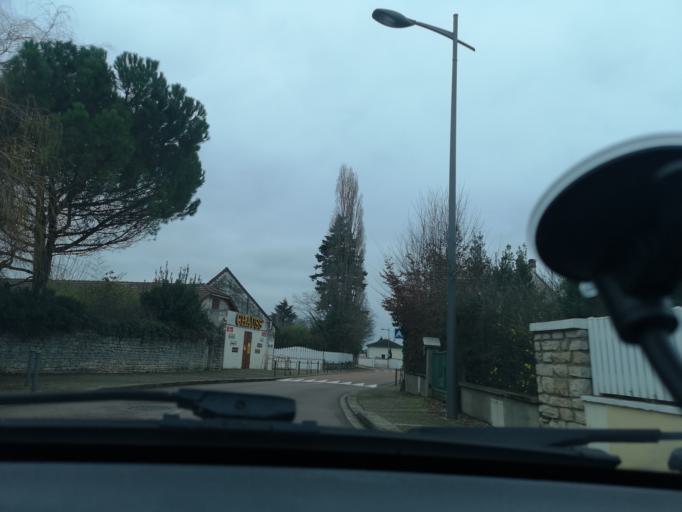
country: FR
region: Bourgogne
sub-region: Departement de Saone-et-Loire
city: Chatenoy-le-Royal
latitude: 46.7904
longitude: 4.8099
